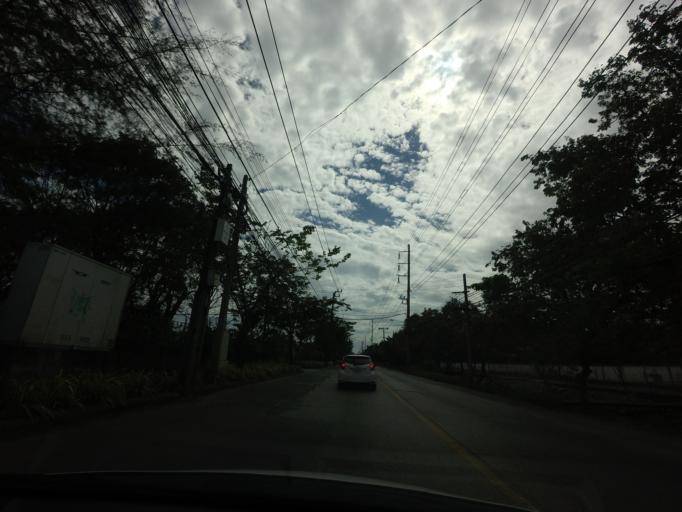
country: TH
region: Bangkok
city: Phra Khanong
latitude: 13.6684
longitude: 100.5917
